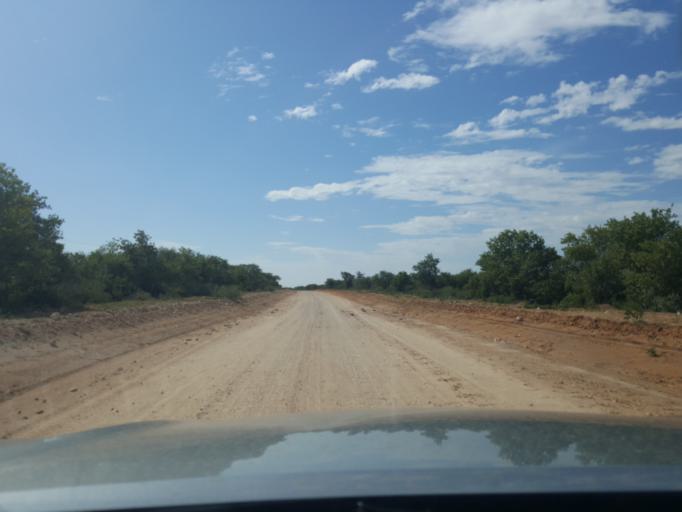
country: BW
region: Kweneng
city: Khudumelapye
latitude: -23.7712
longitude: 24.7668
